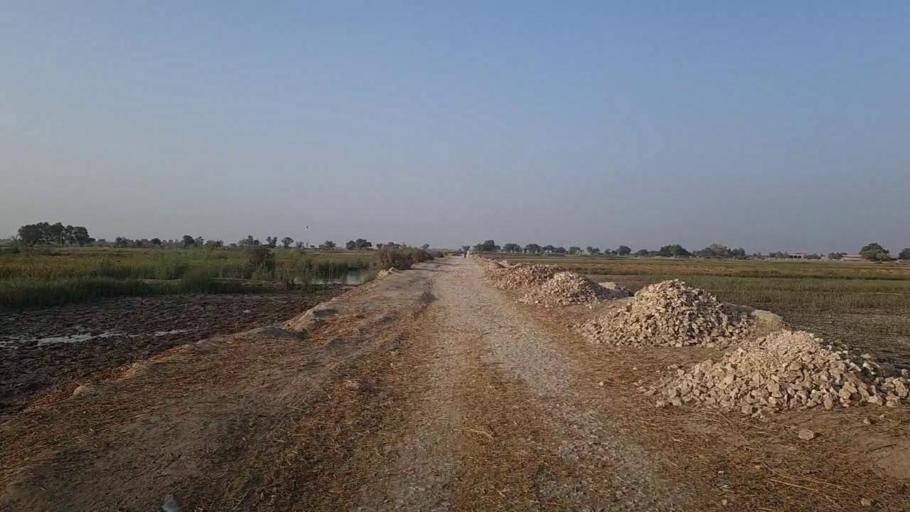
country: PK
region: Sindh
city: Tangwani
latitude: 28.2501
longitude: 69.0690
